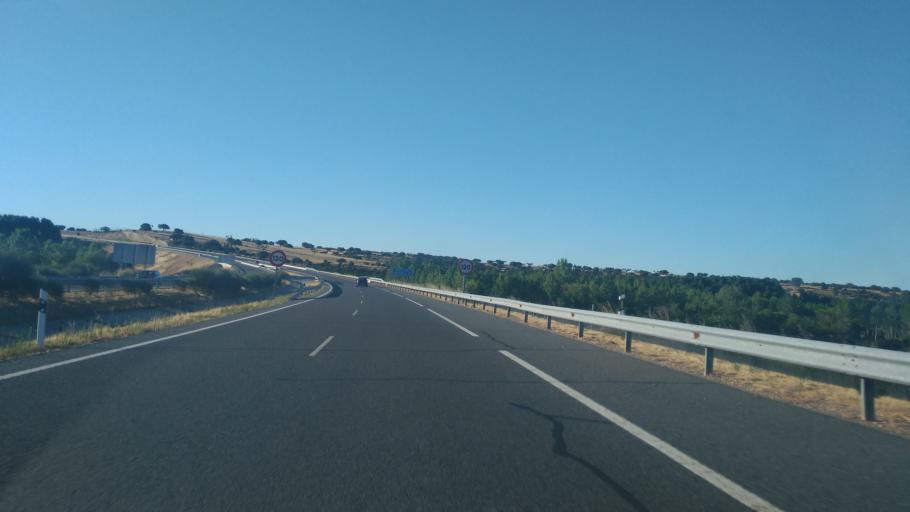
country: ES
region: Castille and Leon
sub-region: Provincia de Salamanca
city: Belena
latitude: 40.7109
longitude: -5.6231
